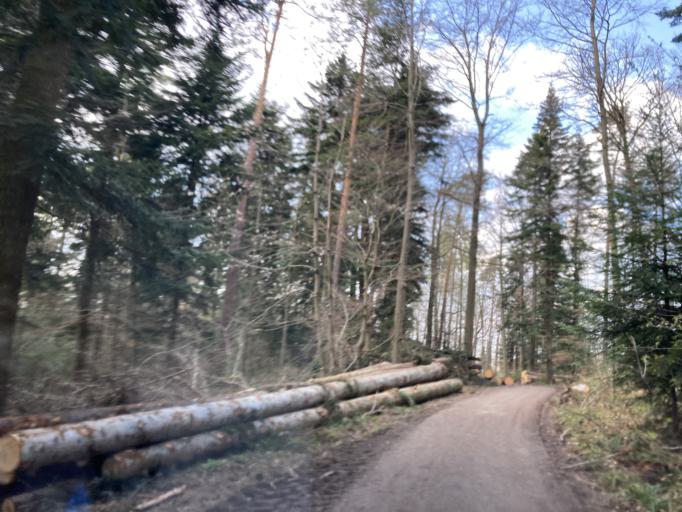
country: DE
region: Baden-Wuerttemberg
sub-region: Karlsruhe Region
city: Dobel
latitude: 48.8385
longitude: 8.5187
